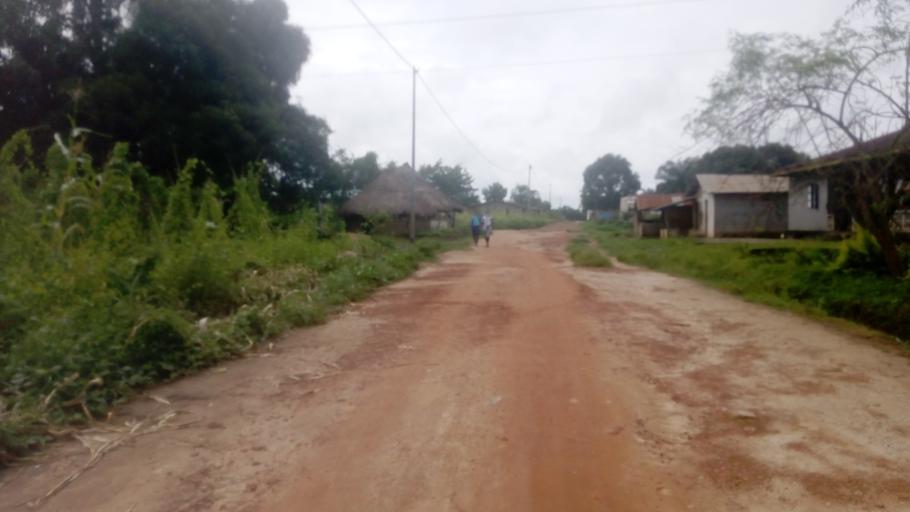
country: SL
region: Northern Province
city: Lunsar
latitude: 8.6926
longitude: -12.5376
